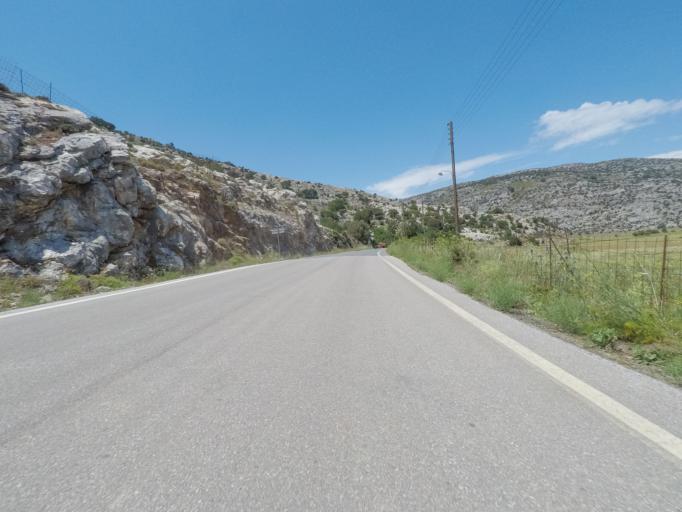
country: GR
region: Crete
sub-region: Nomos Irakleiou
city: Mokhos
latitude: 35.1868
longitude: 25.4314
